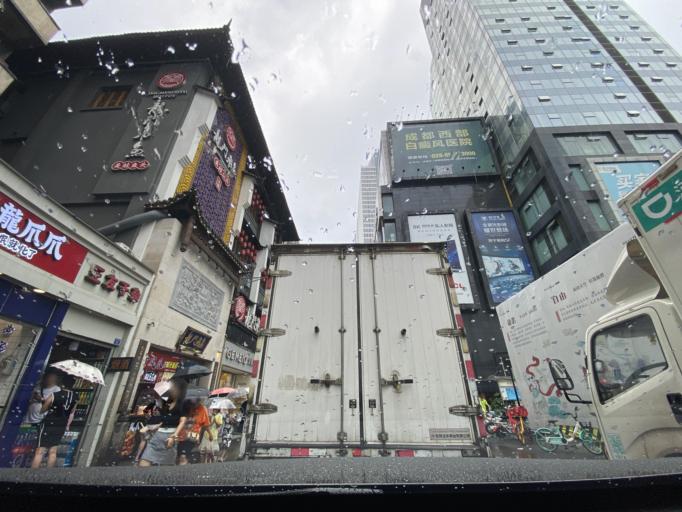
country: CN
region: Sichuan
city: Chengdu
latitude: 30.6566
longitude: 104.0759
